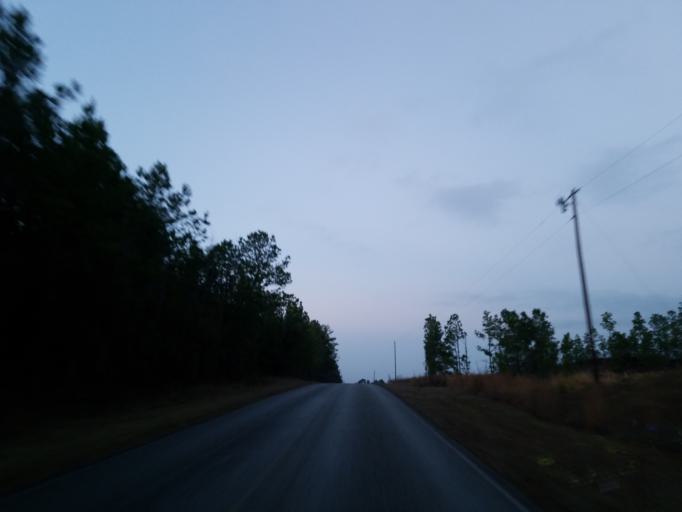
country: US
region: Alabama
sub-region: Sumter County
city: York
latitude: 32.4139
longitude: -88.4385
